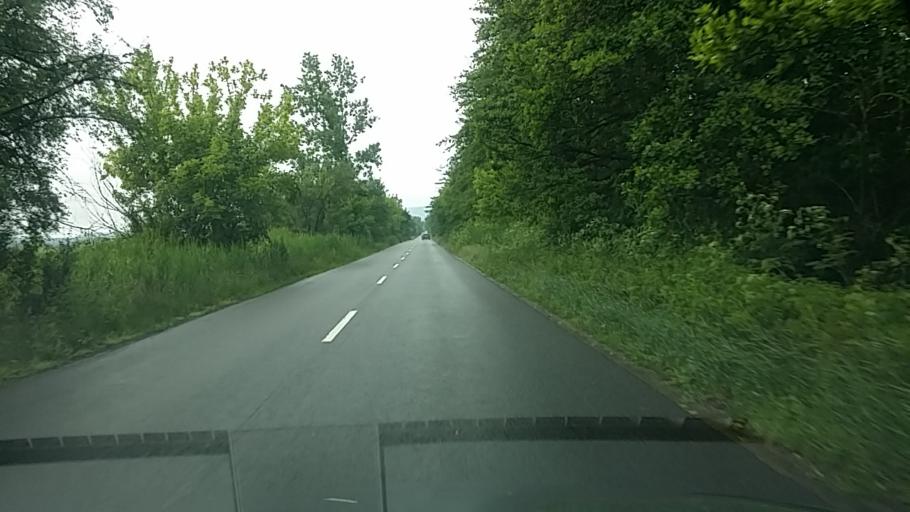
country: HU
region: Komarom-Esztergom
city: Esztergom
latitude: 47.8994
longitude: 18.7753
